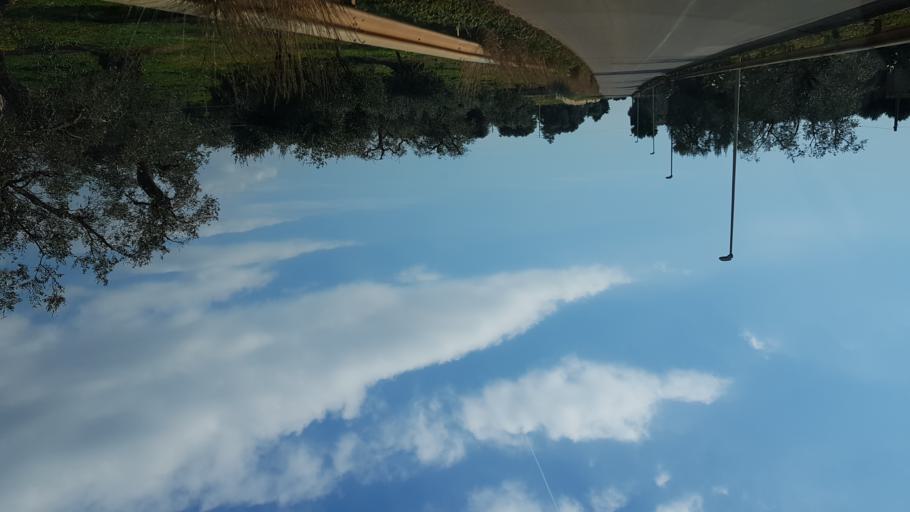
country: IT
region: Apulia
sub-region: Provincia di Brindisi
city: Carovigno
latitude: 40.7134
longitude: 17.6836
